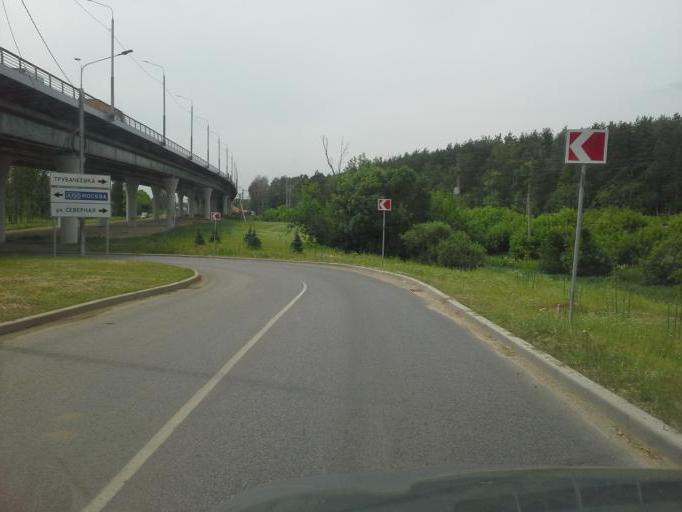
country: RU
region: Moskovskaya
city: Lesnoy Gorodok
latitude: 55.6561
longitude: 37.1707
